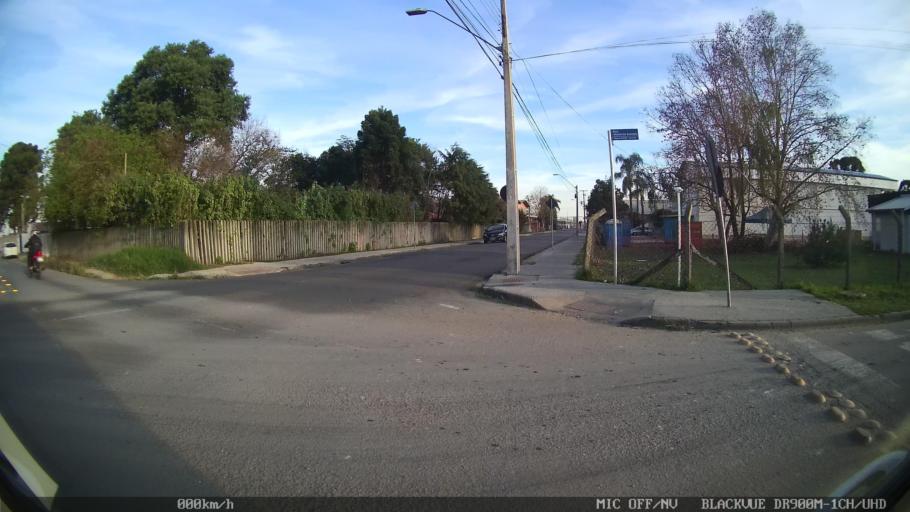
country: BR
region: Parana
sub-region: Pinhais
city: Pinhais
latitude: -25.4422
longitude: -49.1761
